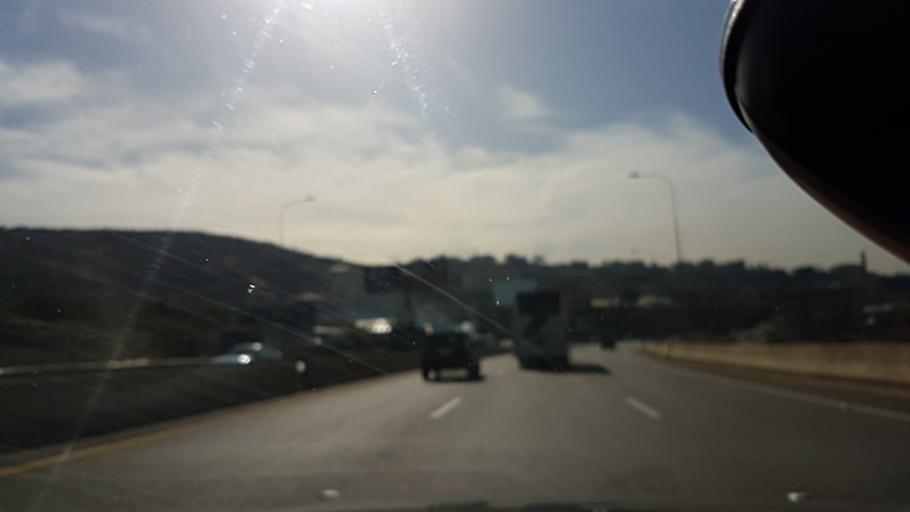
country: LB
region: Liban-Sud
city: Sidon
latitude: 33.6130
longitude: 35.4055
